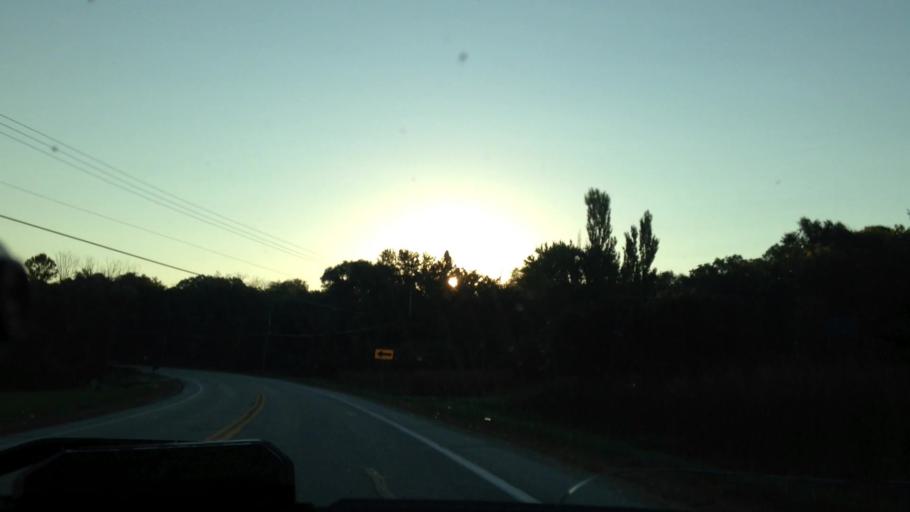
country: US
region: Wisconsin
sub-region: Washington County
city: Newburg
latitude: 43.4231
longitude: -88.0652
